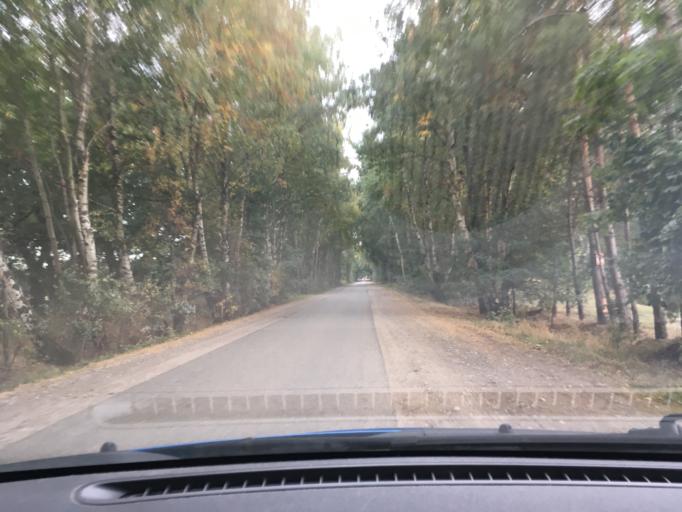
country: DE
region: Lower Saxony
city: Winsen
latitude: 53.3667
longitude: 10.2373
